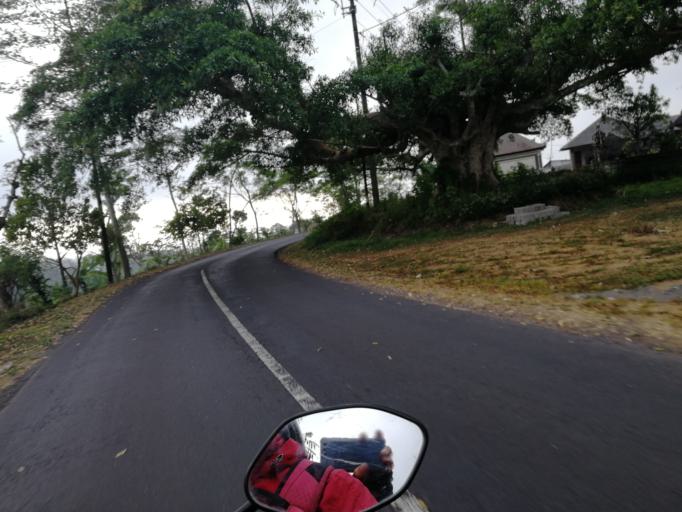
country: ID
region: Bali
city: Banjar Kedisan
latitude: -8.2416
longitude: 115.2431
